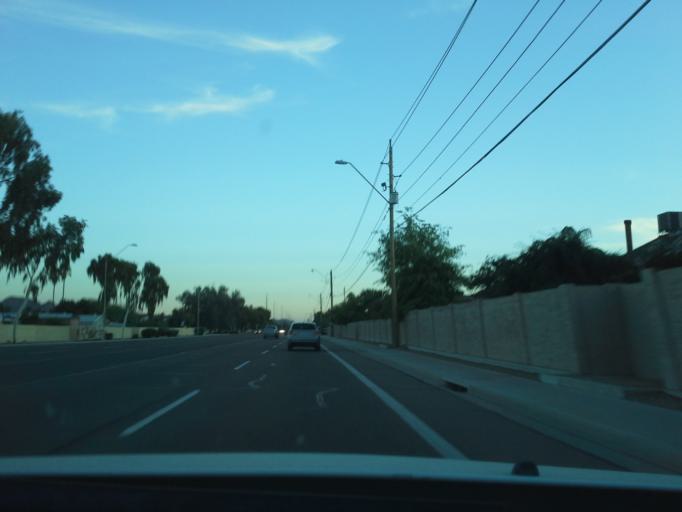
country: US
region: Arizona
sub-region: Maricopa County
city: Glendale
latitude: 33.6602
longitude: -112.0657
